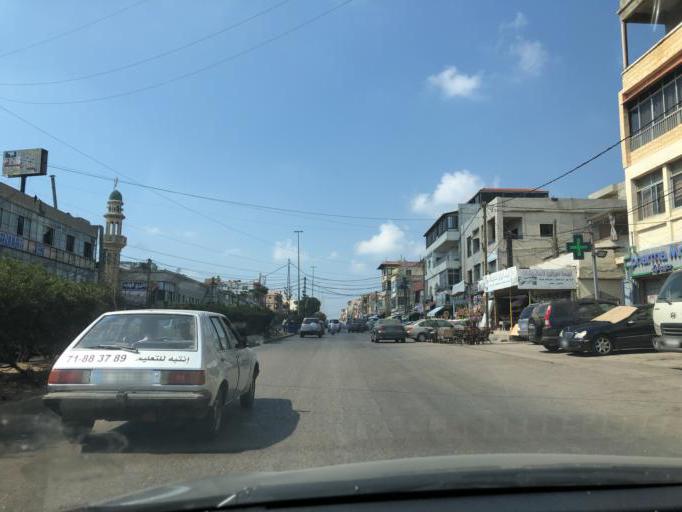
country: LB
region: Beyrouth
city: Beirut
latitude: 33.8427
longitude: 35.4849
